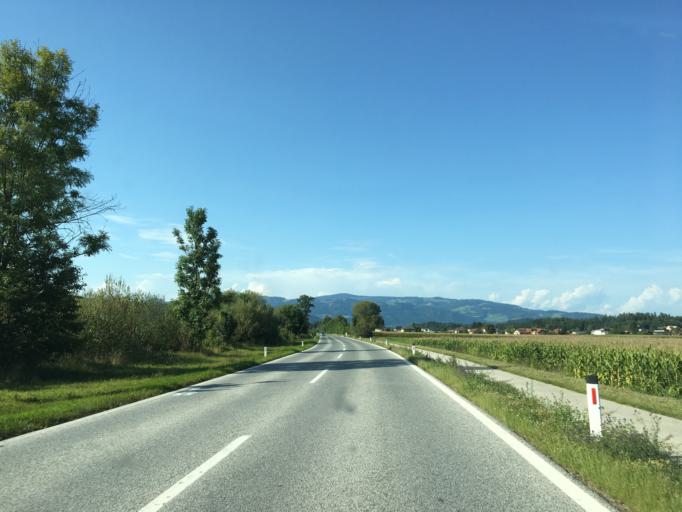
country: AT
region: Carinthia
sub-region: Politischer Bezirk Volkermarkt
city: Eberndorf
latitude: 46.6114
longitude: 14.6359
